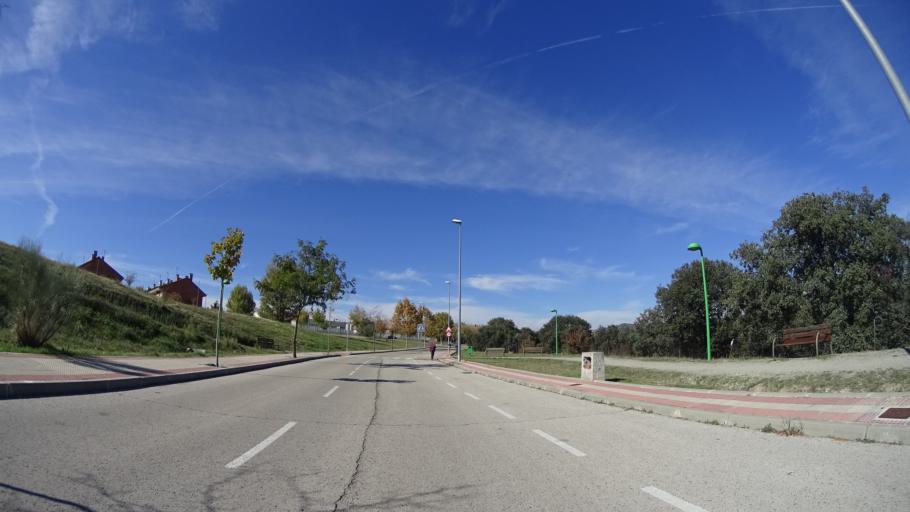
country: ES
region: Madrid
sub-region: Provincia de Madrid
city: Villanueva del Pardillo
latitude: 40.4982
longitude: -3.9635
